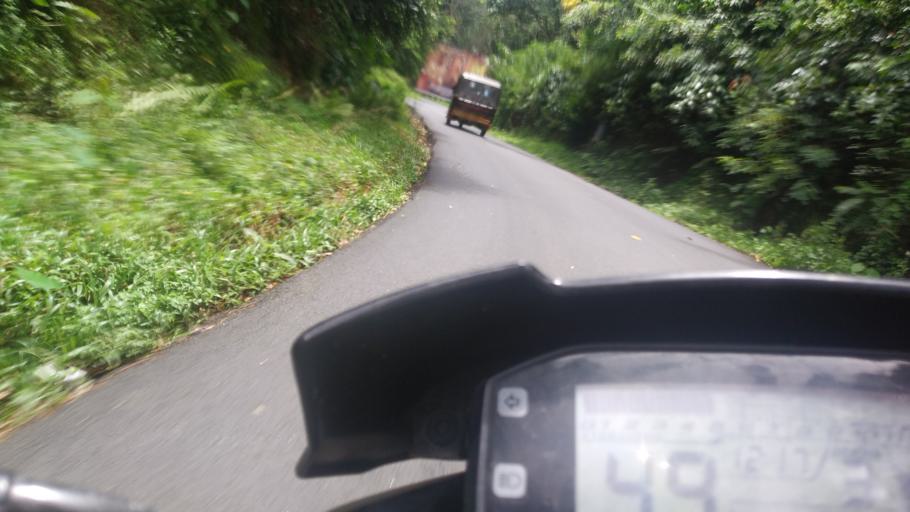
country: IN
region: Kerala
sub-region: Idukki
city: Munnar
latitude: 10.0180
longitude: 77.0090
